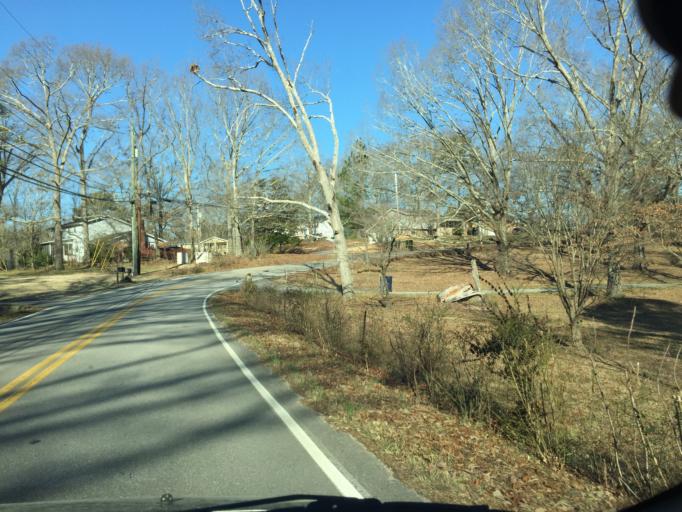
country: US
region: Tennessee
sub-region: Hamilton County
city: Collegedale
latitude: 35.0523
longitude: -85.1109
